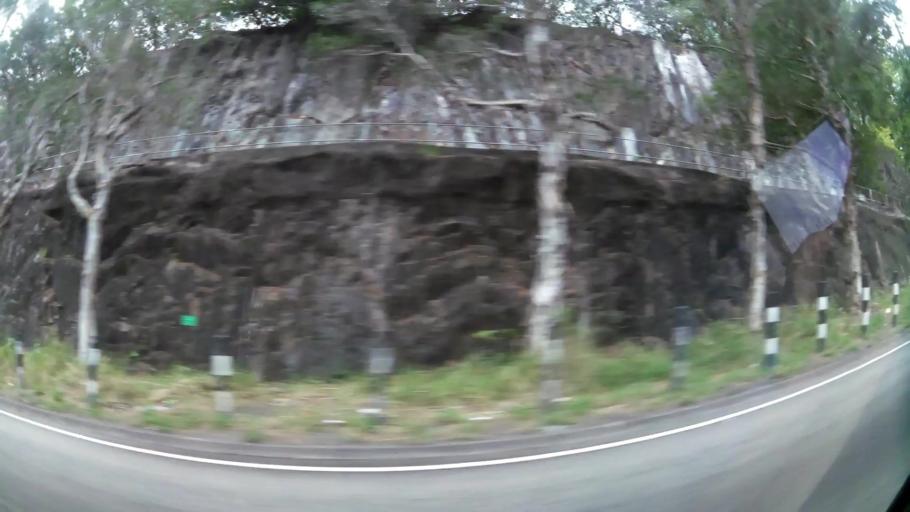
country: HK
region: Tsuen Wan
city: Tsuen Wan
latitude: 22.3624
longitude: 114.1165
